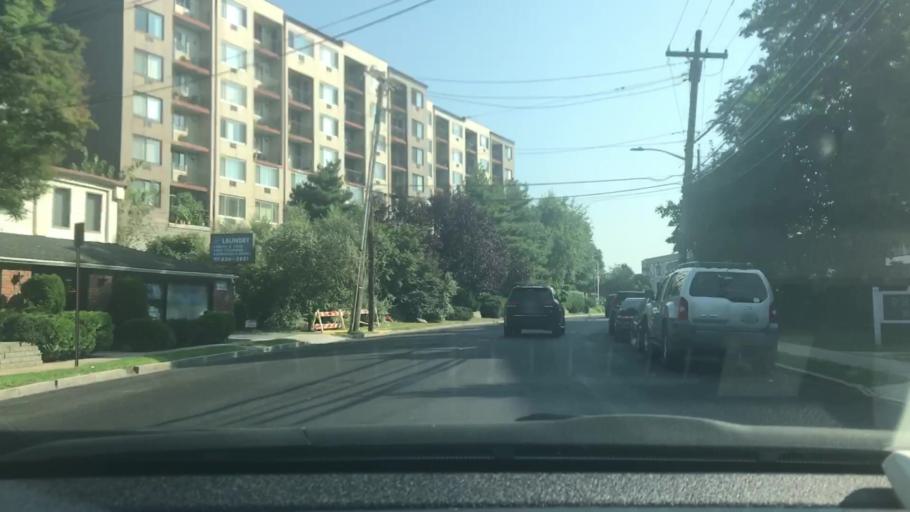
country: US
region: New York
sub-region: Westchester County
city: Pelham Manor
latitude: 40.8884
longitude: -73.7898
